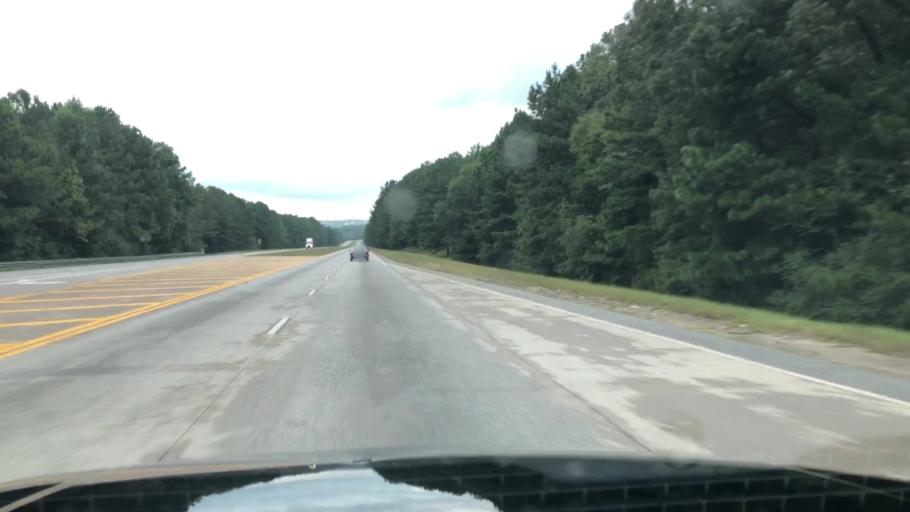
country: US
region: Georgia
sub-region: Cobb County
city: Mableton
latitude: 33.7006
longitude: -84.5768
